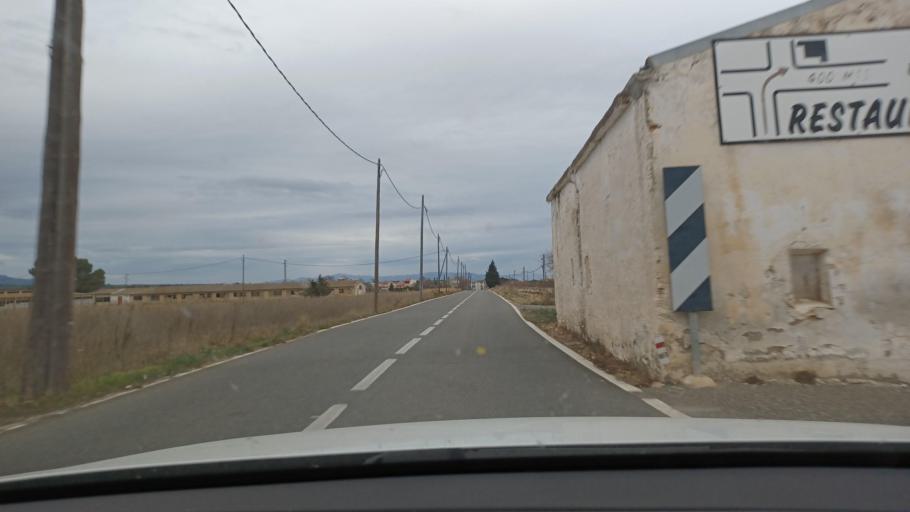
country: ES
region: Catalonia
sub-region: Provincia de Tarragona
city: Ulldecona
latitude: 40.6223
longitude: 0.3624
